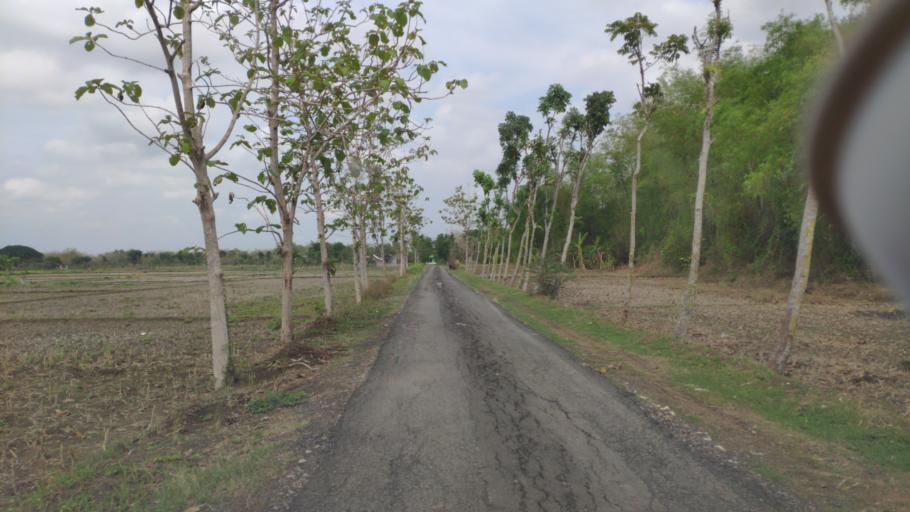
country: ID
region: Central Java
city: Ngablak
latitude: -7.0184
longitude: 111.3840
